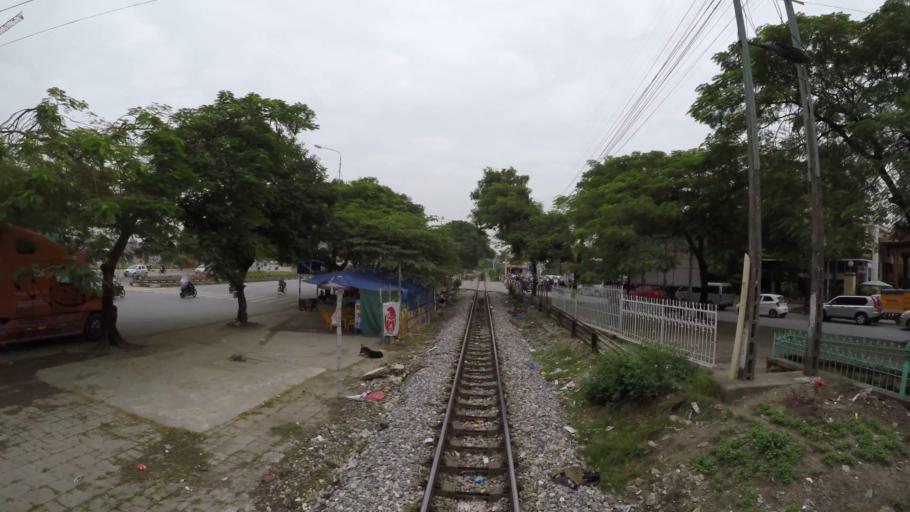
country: VN
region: Hai Phong
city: An Duong
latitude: 20.8761
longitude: 106.6353
